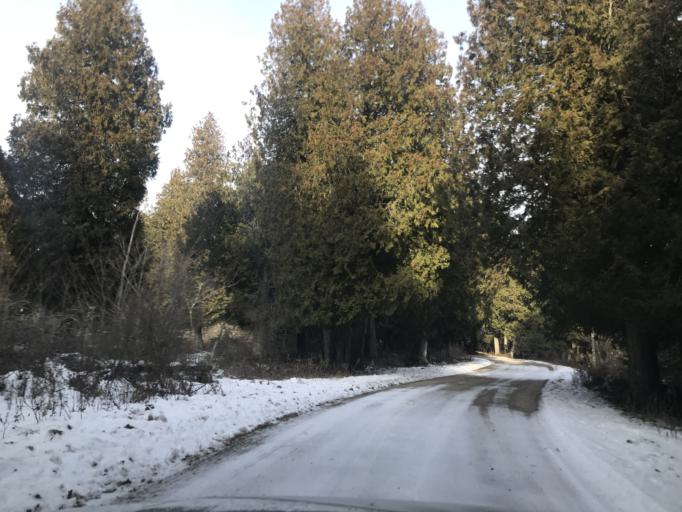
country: US
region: Wisconsin
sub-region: Door County
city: Sturgeon Bay
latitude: 45.1469
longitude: -87.0319
